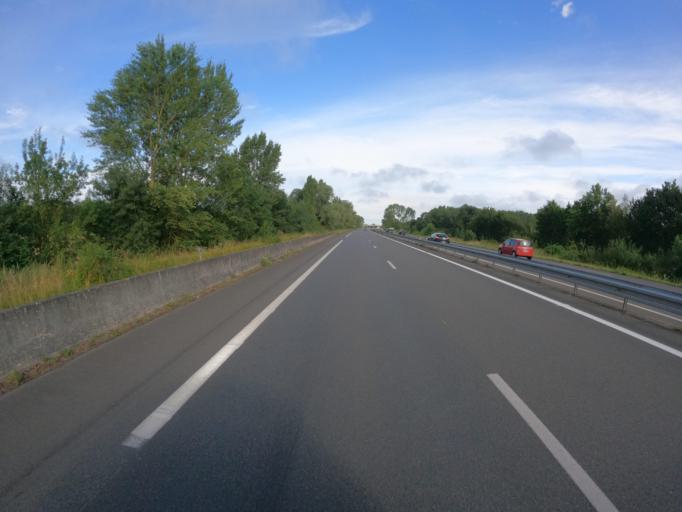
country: FR
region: Pays de la Loire
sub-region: Departement de Maine-et-Loire
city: Allonnes
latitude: 47.2906
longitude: -0.0119
